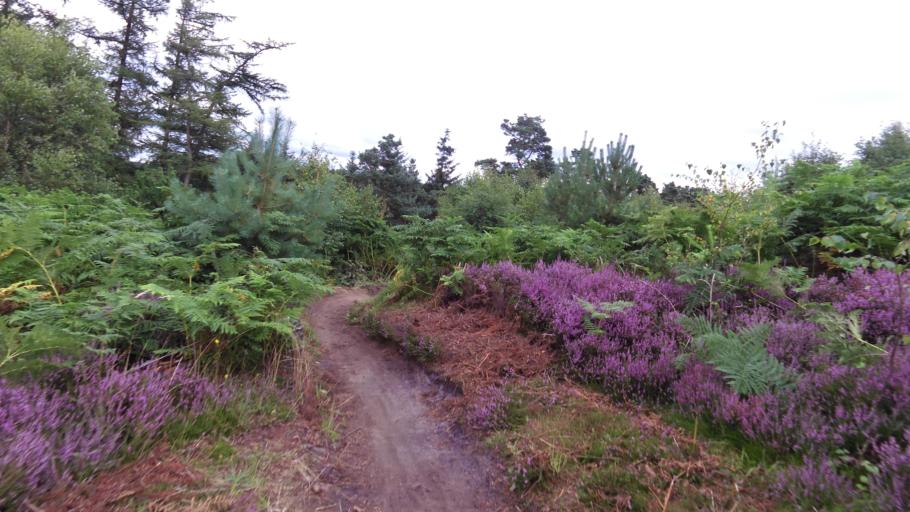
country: GB
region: England
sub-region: North Yorkshire
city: Thornton Dale
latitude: 54.2913
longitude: -0.6811
